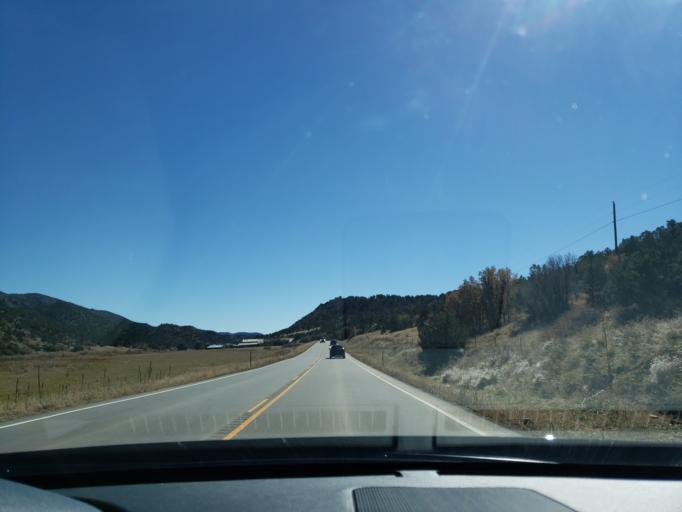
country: US
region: Colorado
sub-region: Fremont County
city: Canon City
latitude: 38.6076
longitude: -105.4380
